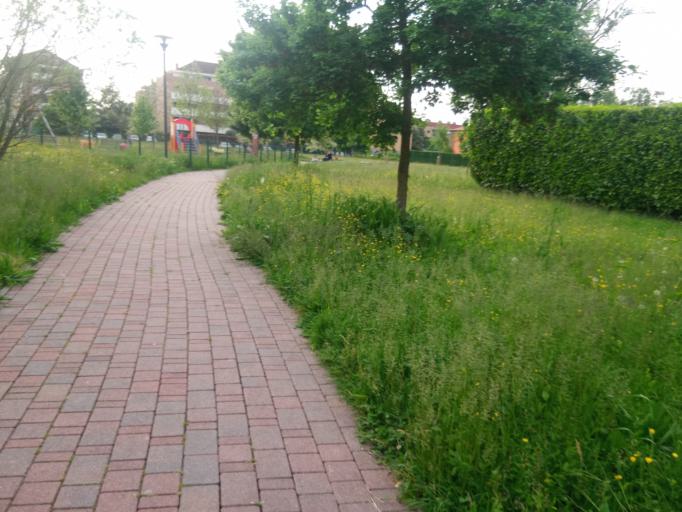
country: IT
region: Veneto
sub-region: Provincia di Padova
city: Mandriola-Sant'Agostino
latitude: 45.3832
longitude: 11.8497
